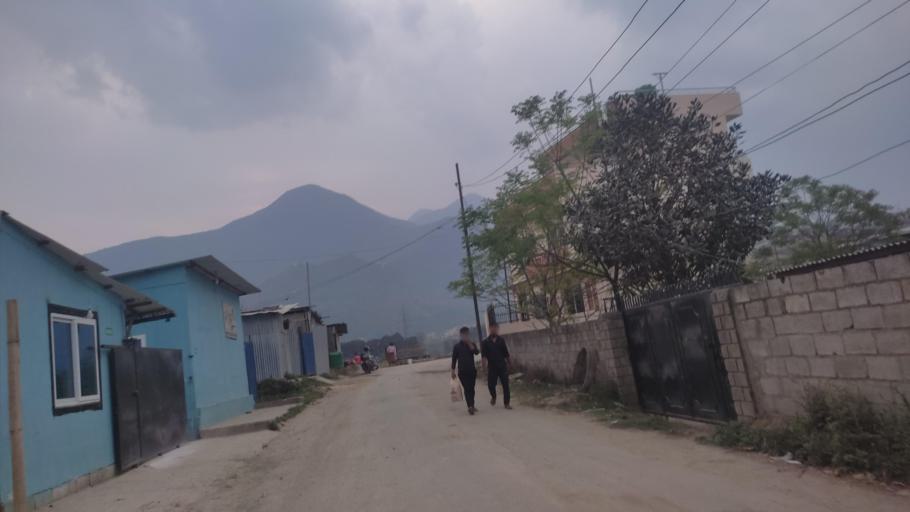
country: NP
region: Central Region
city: Kirtipur
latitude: 27.6596
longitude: 85.2861
